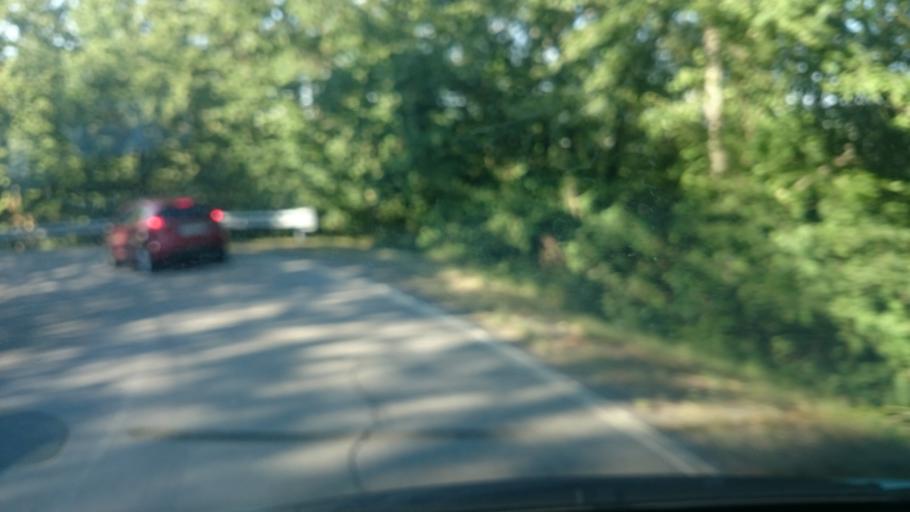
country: IT
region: Emilia-Romagna
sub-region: Provincia di Reggio Emilia
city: Villa Minozzo
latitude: 44.3709
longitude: 10.4609
